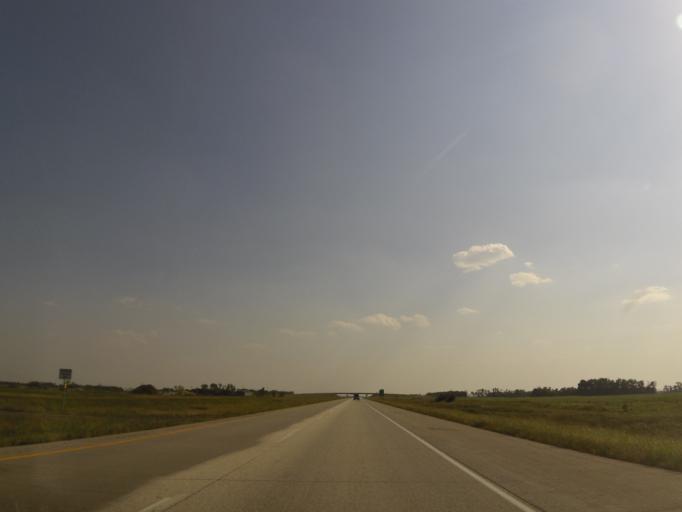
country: US
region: North Dakota
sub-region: Walsh County
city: Grafton
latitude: 48.3036
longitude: -97.1895
